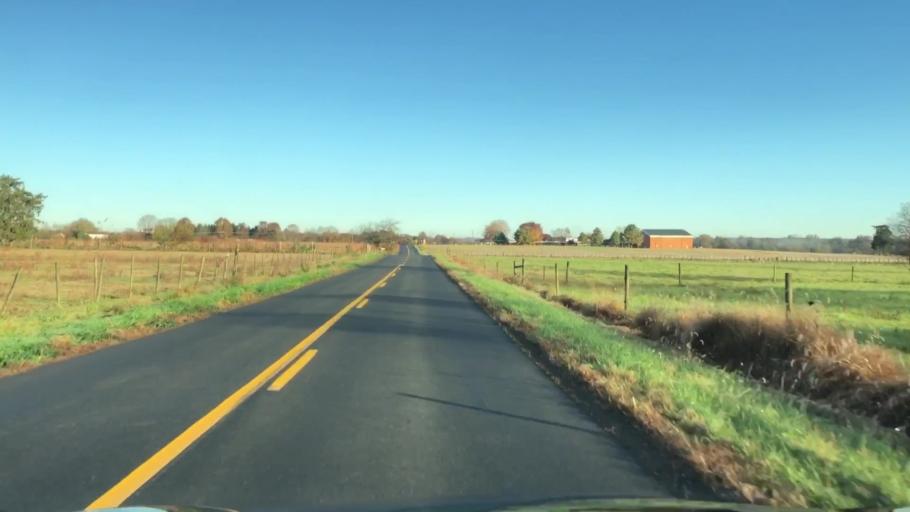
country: US
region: Virginia
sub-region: Prince William County
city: Nokesville
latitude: 38.6444
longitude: -77.6766
